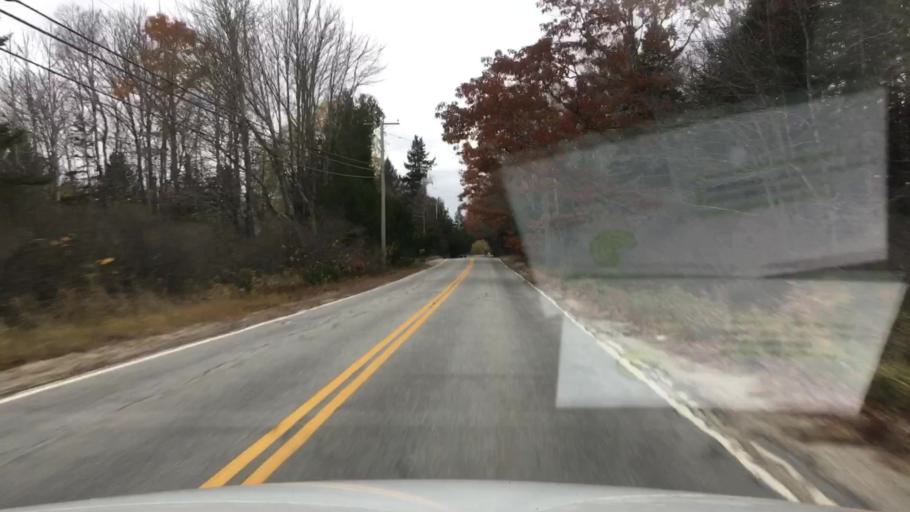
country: US
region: Maine
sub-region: Hancock County
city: Sedgwick
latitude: 44.3690
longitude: -68.5555
